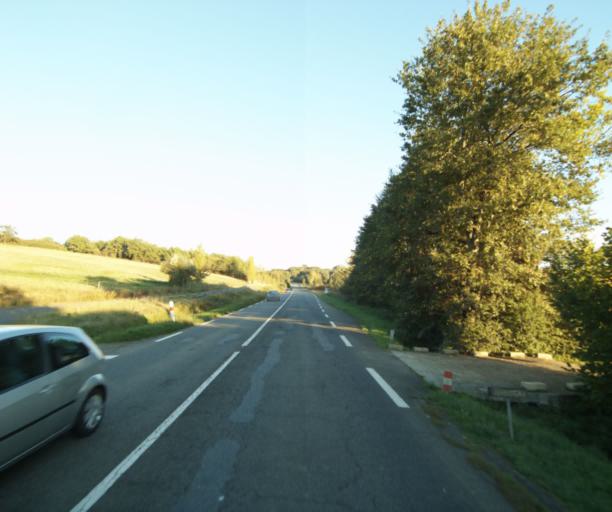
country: FR
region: Midi-Pyrenees
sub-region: Departement du Gers
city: Eauze
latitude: 43.7620
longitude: 0.1787
